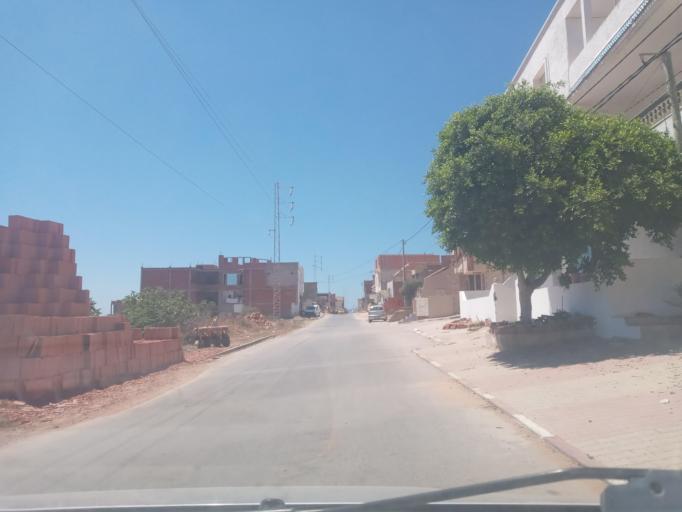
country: TN
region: Nabul
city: El Haouaria
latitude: 37.0494
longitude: 11.0043
